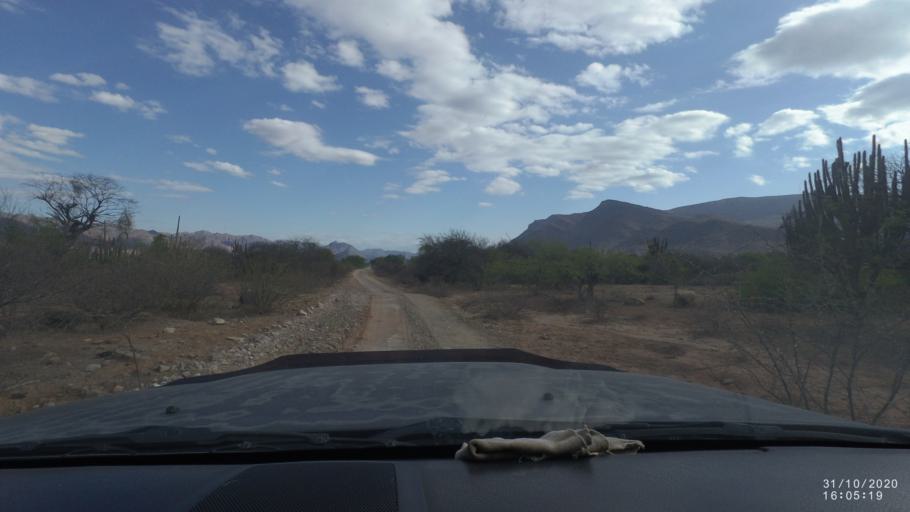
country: BO
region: Chuquisaca
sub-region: Provincia Zudanez
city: Mojocoya
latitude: -18.3655
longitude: -64.6497
